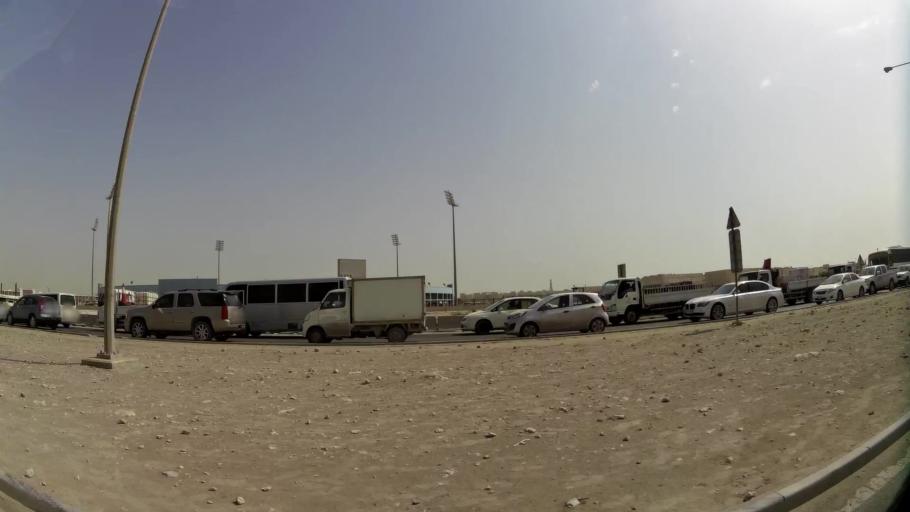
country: QA
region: Al Wakrah
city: Al Wukayr
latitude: 25.1874
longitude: 51.4588
